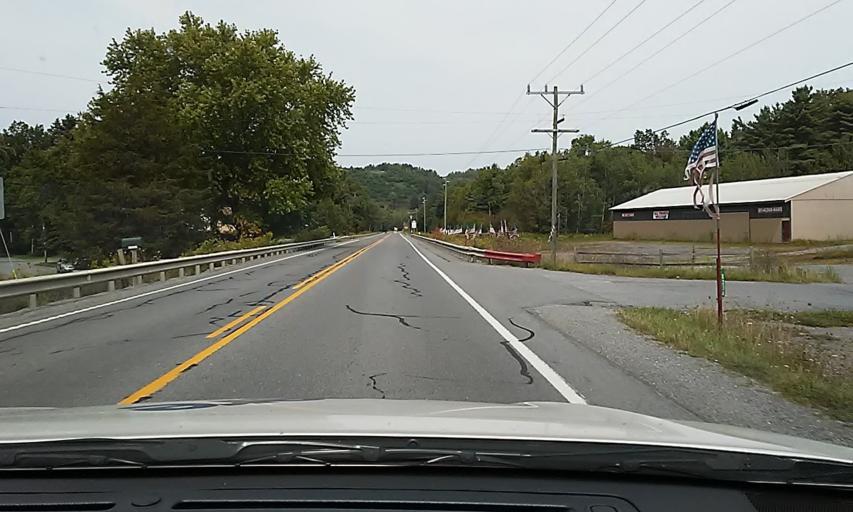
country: US
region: Pennsylvania
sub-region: Clearfield County
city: Treasure Lake
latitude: 41.2740
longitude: -78.6944
